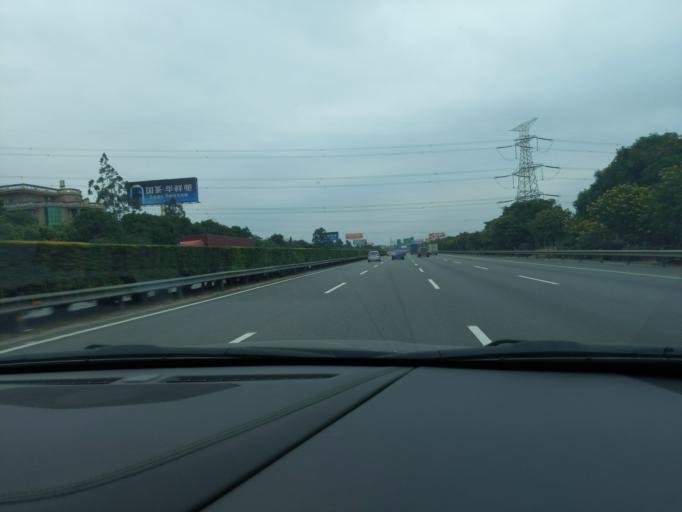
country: CN
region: Fujian
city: Neikeng
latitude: 24.7589
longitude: 118.4467
